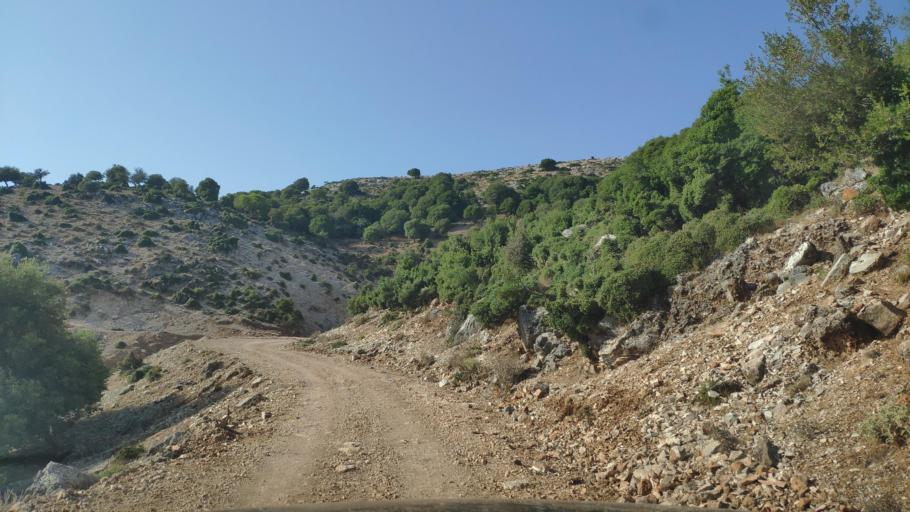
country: GR
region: West Greece
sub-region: Nomos Aitolias kai Akarnanias
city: Monastirakion
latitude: 38.8320
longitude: 20.9730
